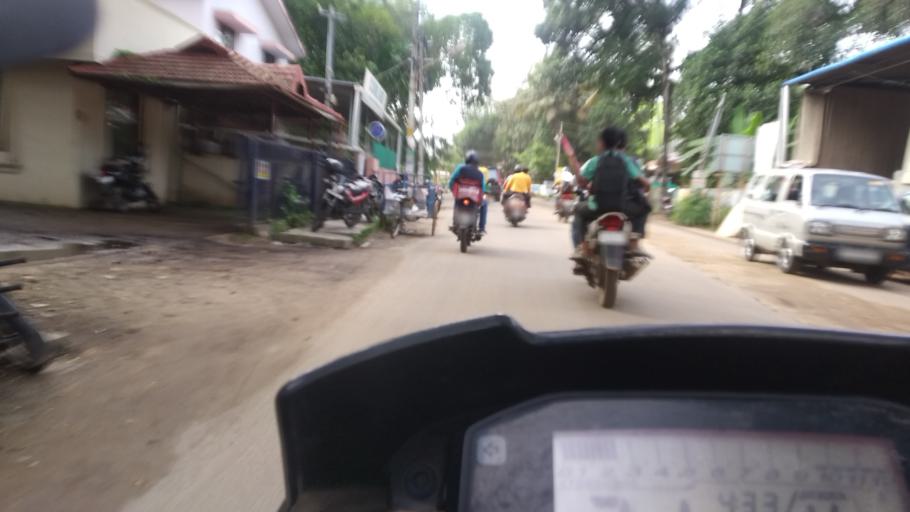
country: IN
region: Kerala
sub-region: Ernakulam
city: Cochin
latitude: 9.9788
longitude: 76.3141
